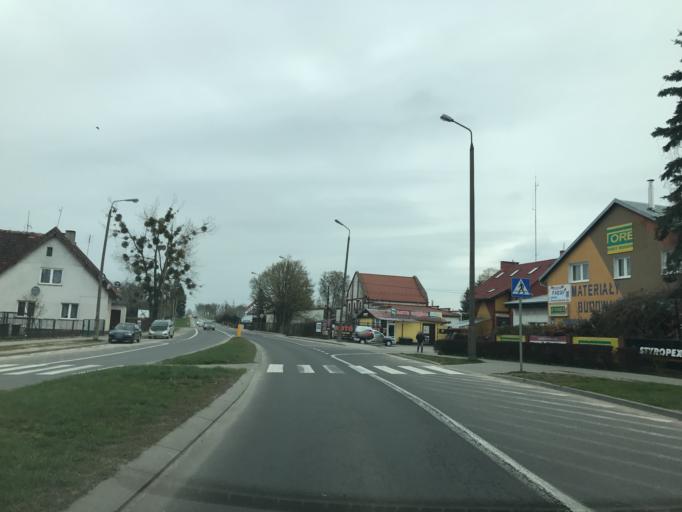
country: PL
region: Warmian-Masurian Voivodeship
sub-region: Powiat olsztynski
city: Olsztynek
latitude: 53.5865
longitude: 20.2894
